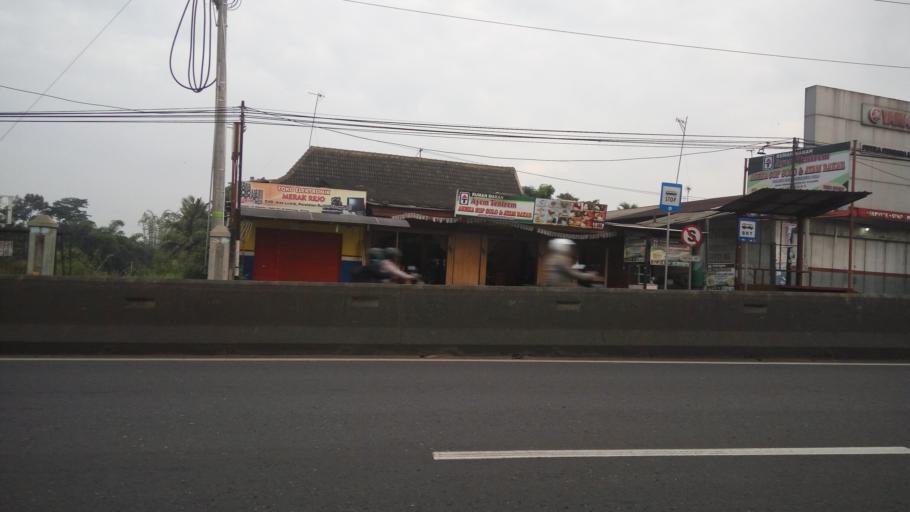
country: ID
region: Central Java
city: Ambarawa
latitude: -7.2259
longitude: 110.4311
